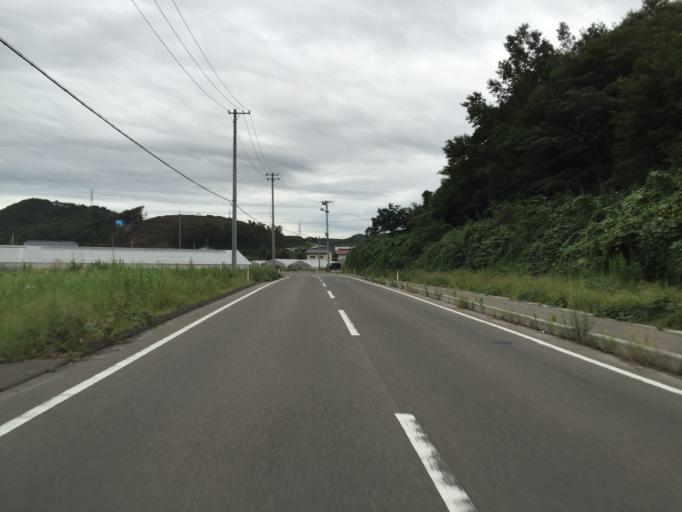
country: JP
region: Fukushima
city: Hobaramachi
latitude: 37.7879
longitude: 140.5123
